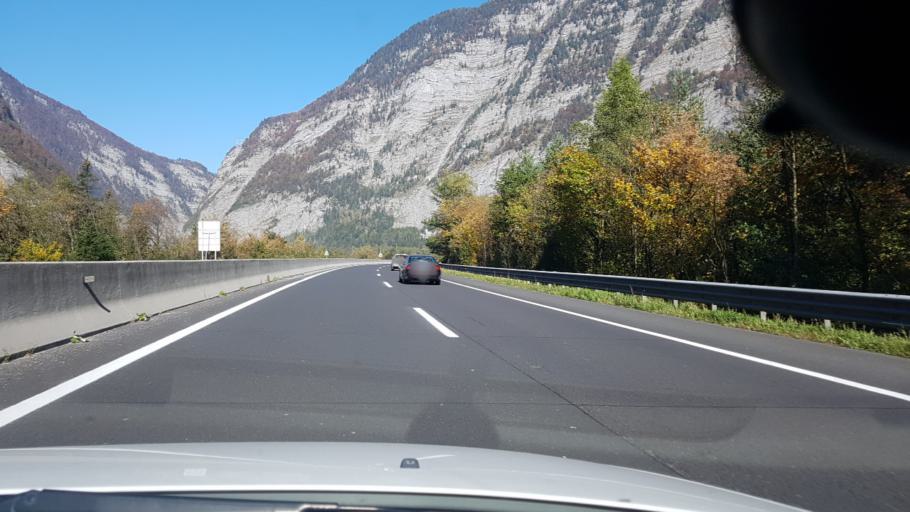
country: AT
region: Salzburg
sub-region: Politischer Bezirk Sankt Johann im Pongau
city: Werfen
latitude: 47.5316
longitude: 13.1696
